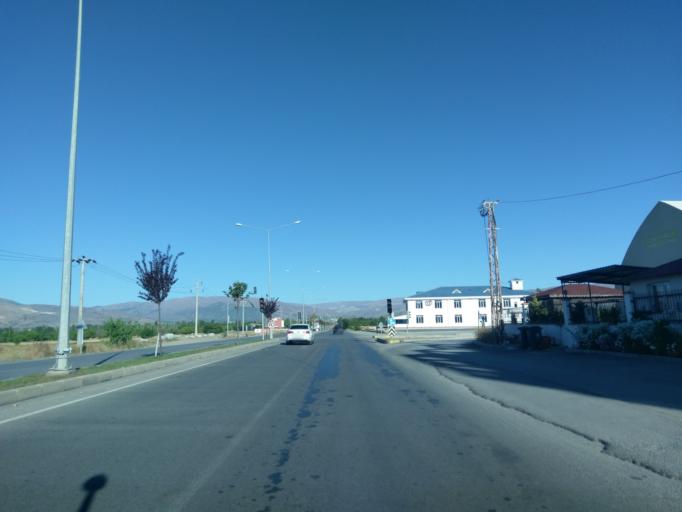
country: TR
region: Erzincan
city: Erzincan
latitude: 39.7652
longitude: 39.4345
